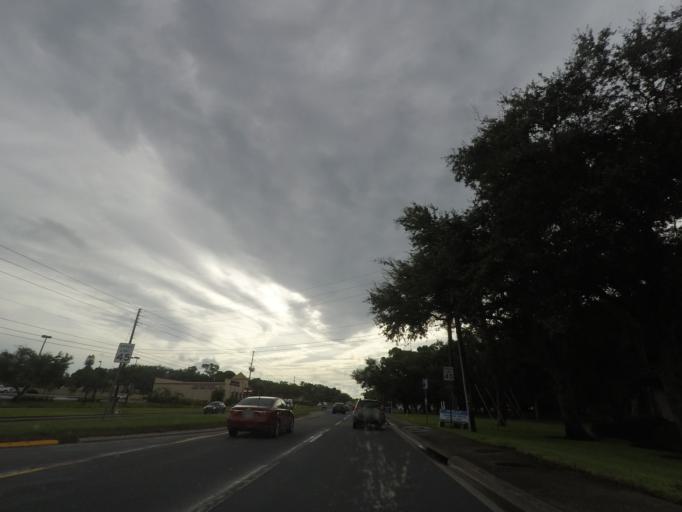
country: US
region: Florida
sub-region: Pinellas County
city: Redington Shores
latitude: 27.8436
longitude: -82.8187
